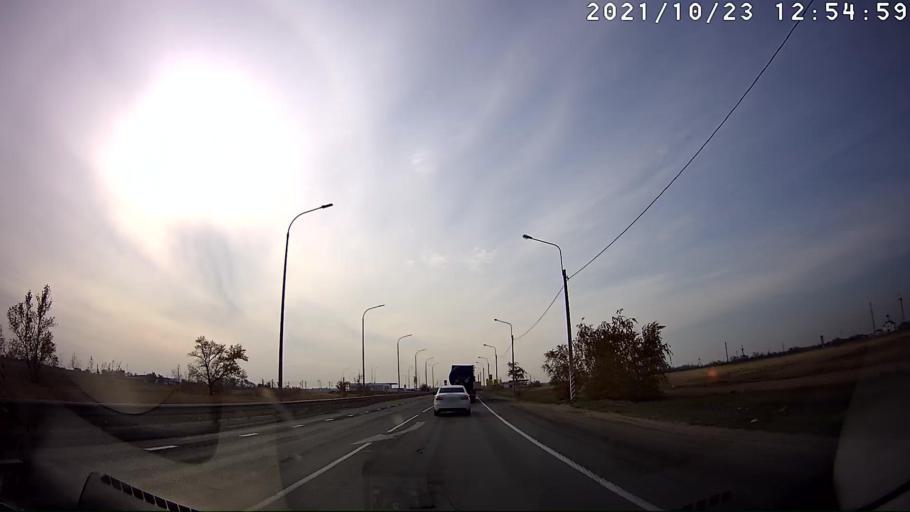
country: RU
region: Volgograd
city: Dubovka
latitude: 49.0536
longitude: 44.7944
